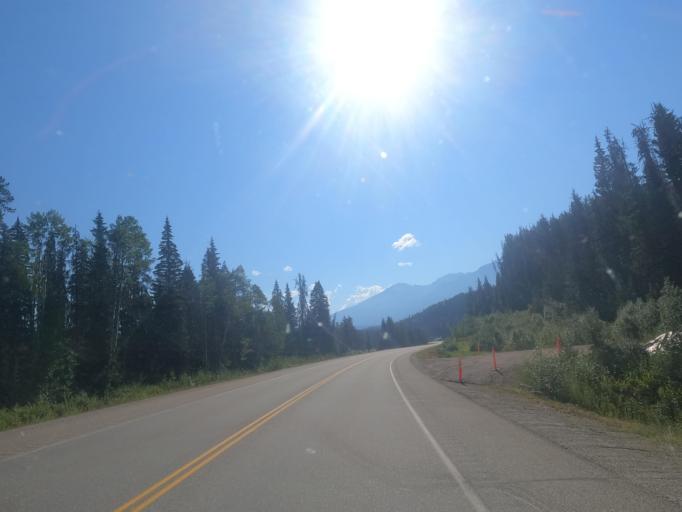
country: CA
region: Alberta
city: Jasper Park Lodge
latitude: 52.8619
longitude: -118.6426
